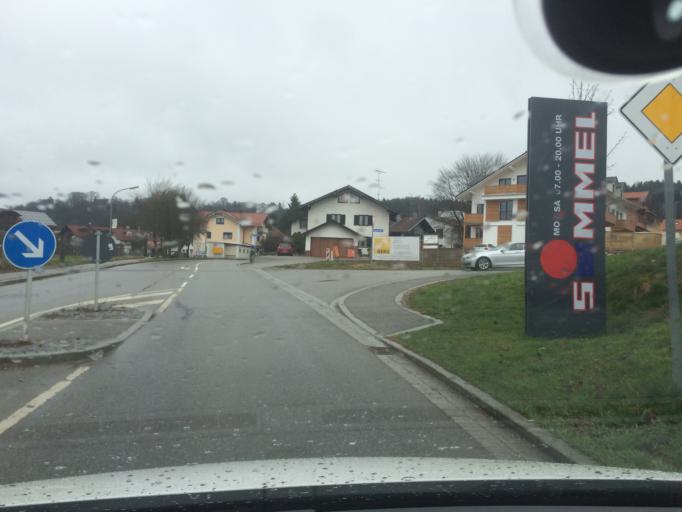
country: DE
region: Bavaria
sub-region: Upper Bavaria
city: Glonn
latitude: 47.9874
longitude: 11.8715
